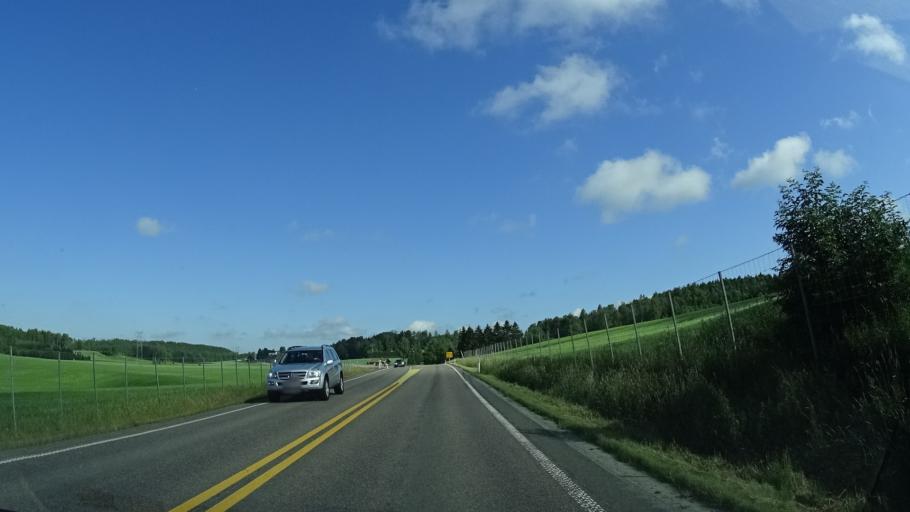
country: NO
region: Ostfold
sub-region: Hobol
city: Elvestad
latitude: 59.6523
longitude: 10.9209
